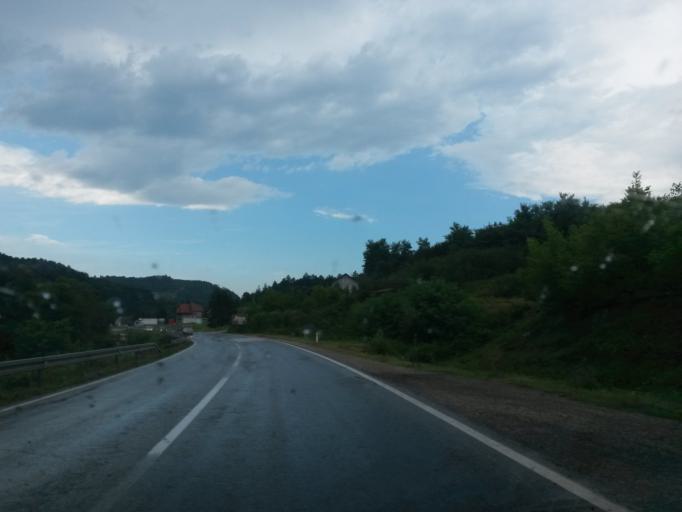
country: BA
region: Federation of Bosnia and Herzegovina
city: Lijesnica
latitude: 44.4919
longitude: 18.0847
